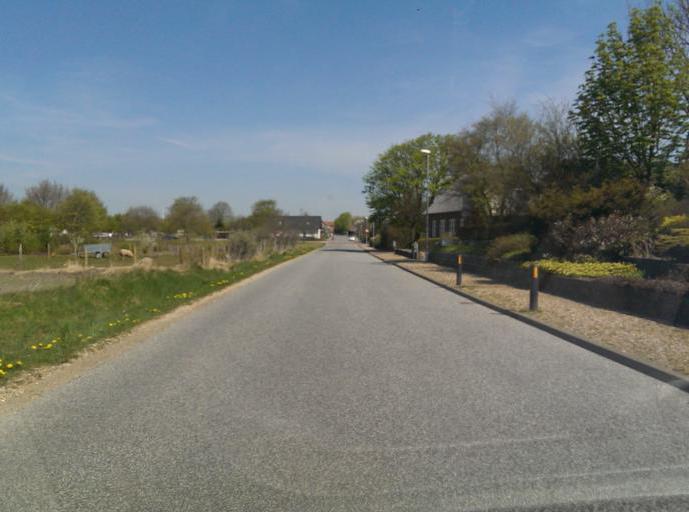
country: DK
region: South Denmark
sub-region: Esbjerg Kommune
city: Tjaereborg
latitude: 55.4600
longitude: 8.5836
